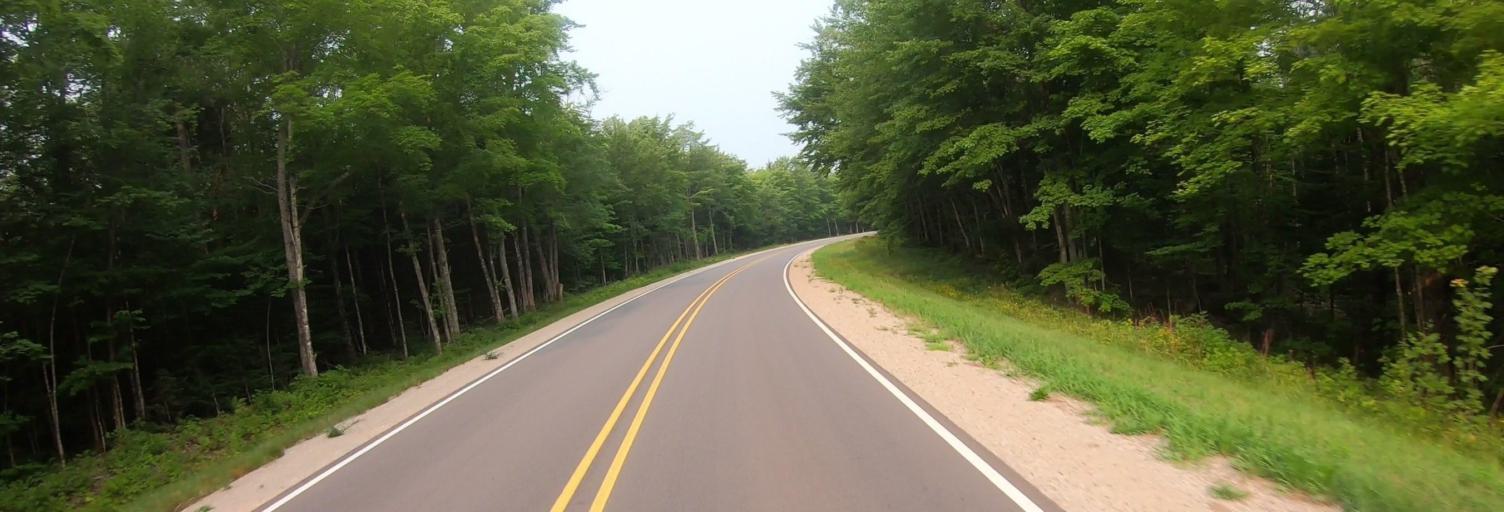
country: US
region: Michigan
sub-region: Luce County
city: Newberry
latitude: 46.4849
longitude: -85.0958
